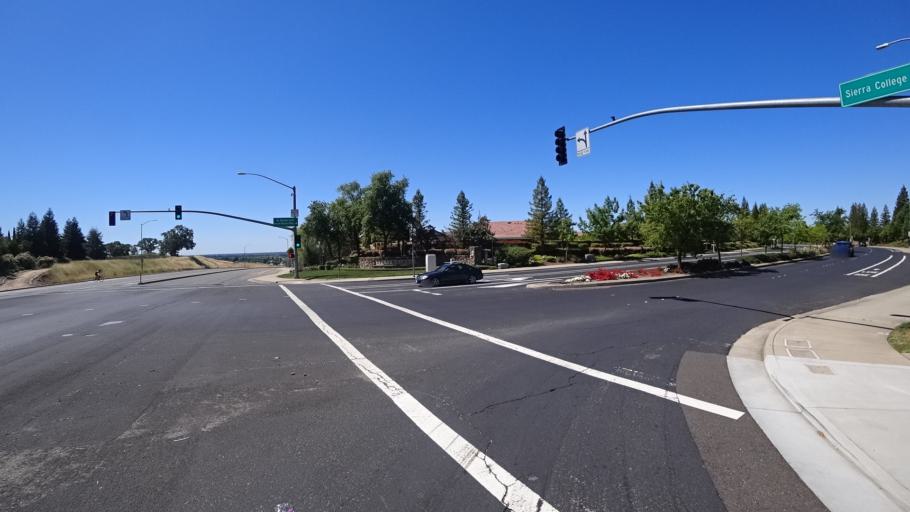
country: US
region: California
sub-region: Placer County
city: Rocklin
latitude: 38.7650
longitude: -121.2229
